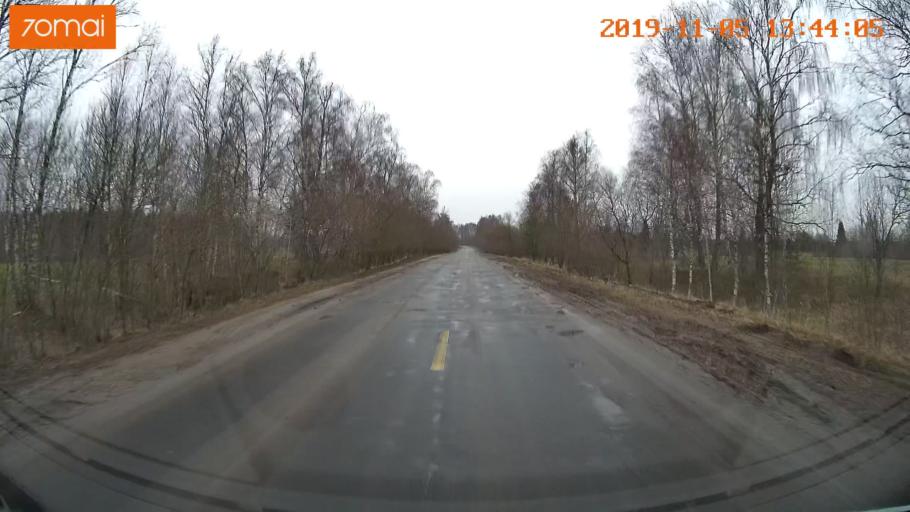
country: RU
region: Ivanovo
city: Shuya
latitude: 56.9784
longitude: 41.4081
